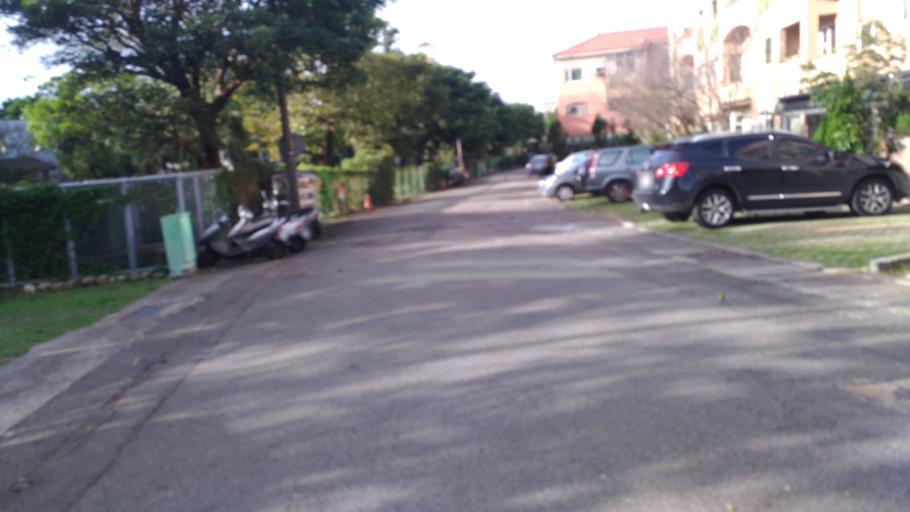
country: TW
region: Taiwan
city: Daxi
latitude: 24.8839
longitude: 121.1728
